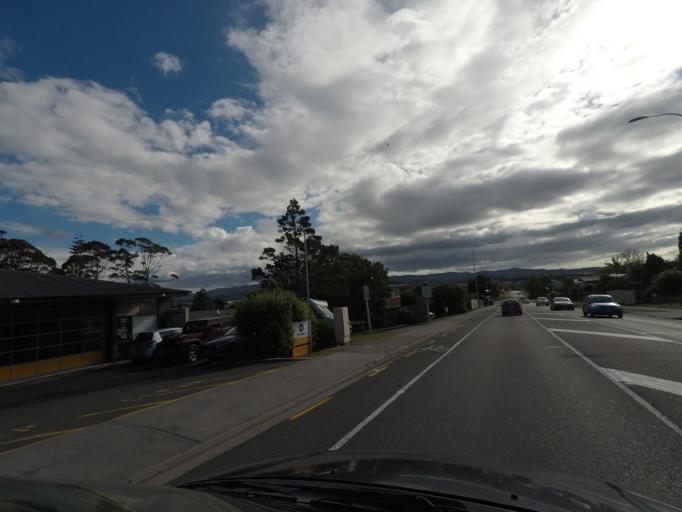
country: NZ
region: Auckland
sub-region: Auckland
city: Rosebank
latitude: -36.8655
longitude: 174.6448
